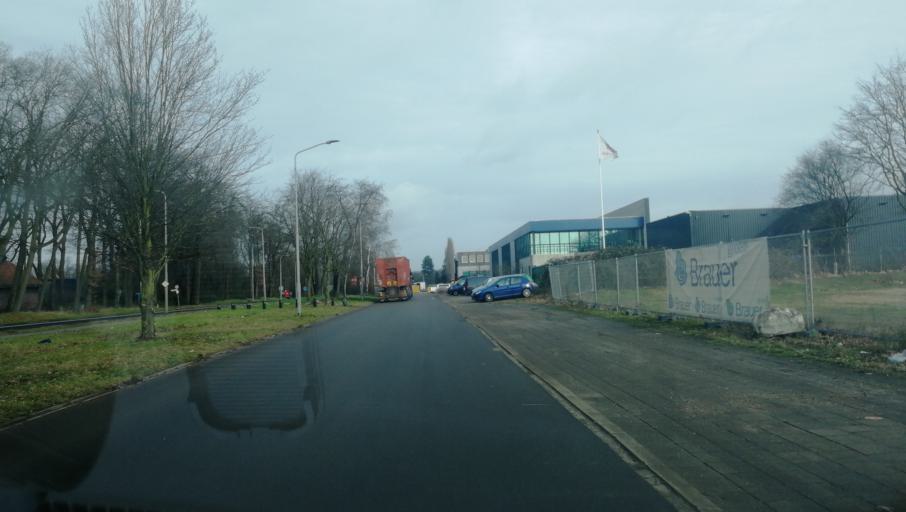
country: NL
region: Limburg
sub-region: Gemeente Venlo
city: Tegelen
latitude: 51.3180
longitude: 6.1153
